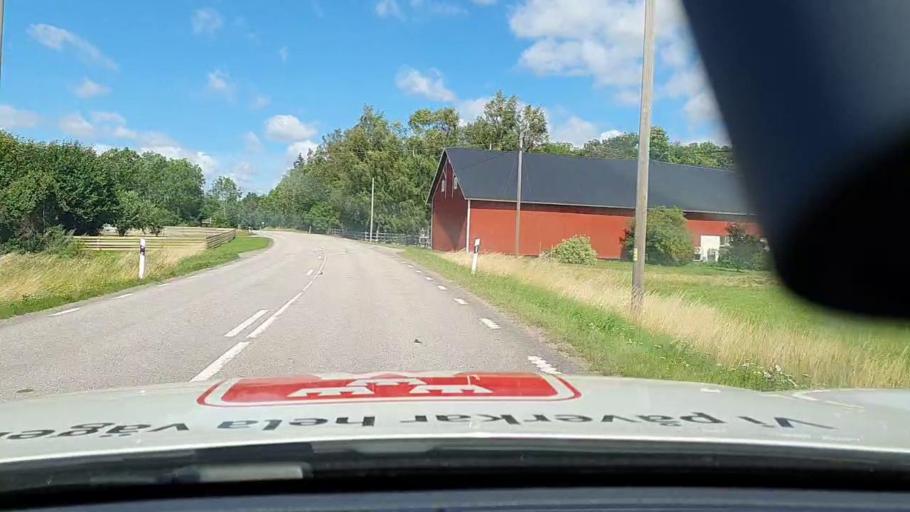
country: SE
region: Vaestra Goetaland
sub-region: Skovde Kommun
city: Stopen
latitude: 58.5167
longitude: 13.9781
